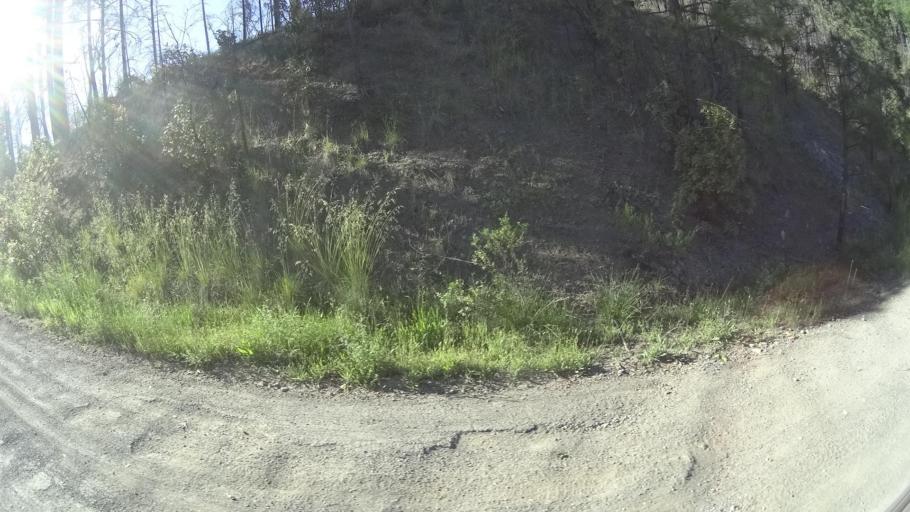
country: US
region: California
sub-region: Lake County
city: Upper Lake
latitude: 39.4034
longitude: -122.9650
